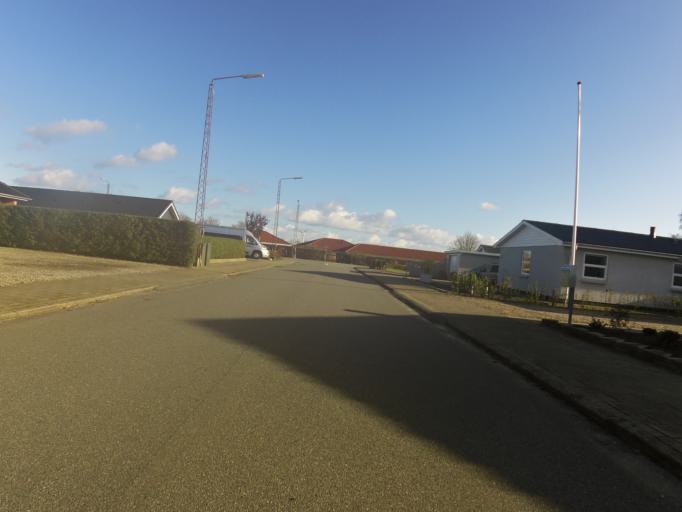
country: DK
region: South Denmark
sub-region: Tonder Kommune
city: Sherrebek
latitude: 55.1517
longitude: 8.7756
